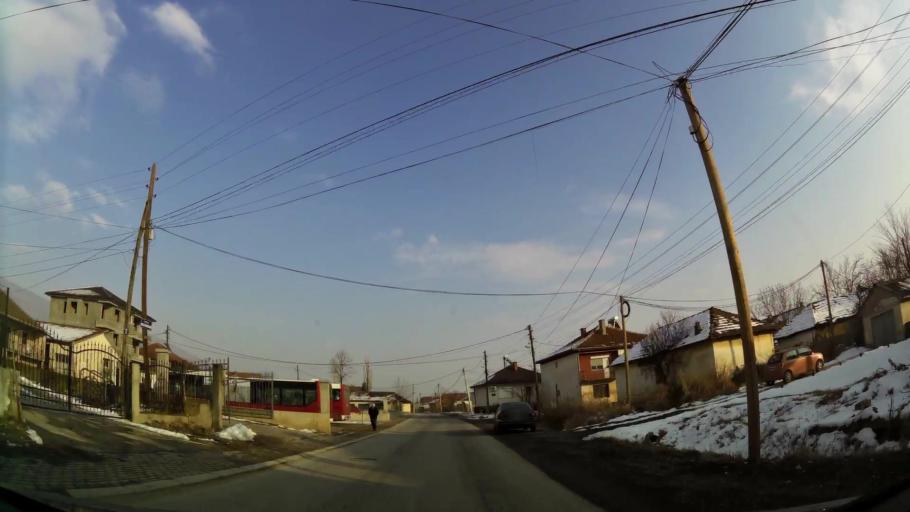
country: MK
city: Creshevo
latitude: 42.0278
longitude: 21.5176
